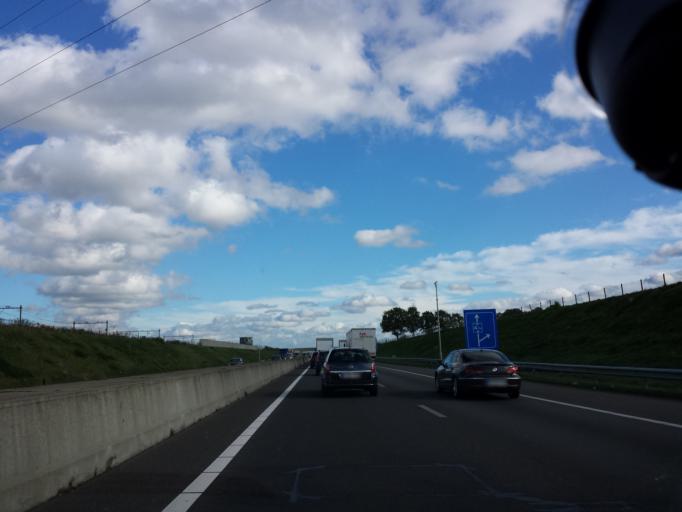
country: NL
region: Limburg
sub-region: Gemeente Roerdalen
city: Montfort
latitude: 51.1571
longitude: 5.9535
